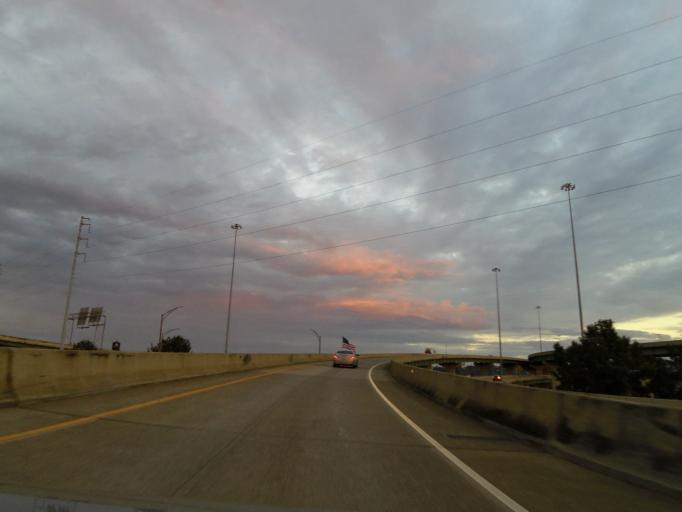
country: US
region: Alabama
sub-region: Jefferson County
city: Birmingham
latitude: 33.5273
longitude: -86.8036
